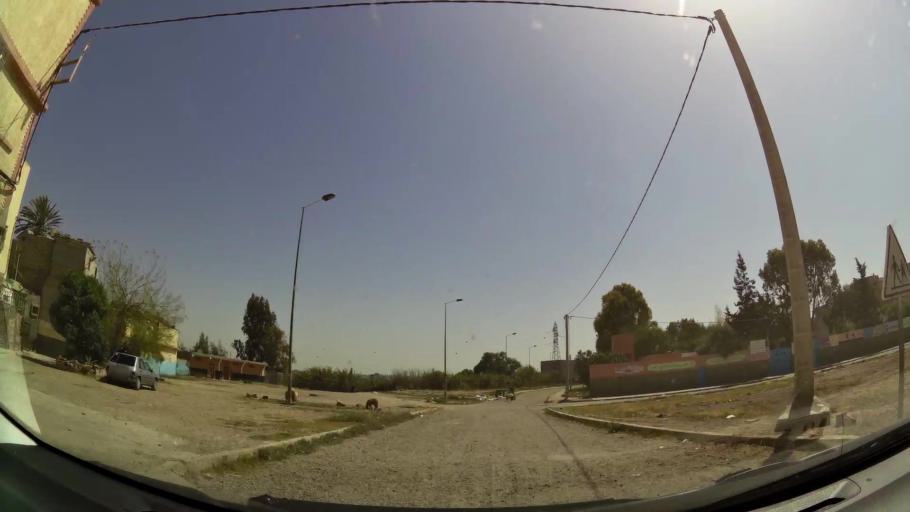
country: MA
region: Souss-Massa-Draa
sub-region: Inezgane-Ait Mellou
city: Inezgane
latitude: 30.3471
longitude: -9.5343
